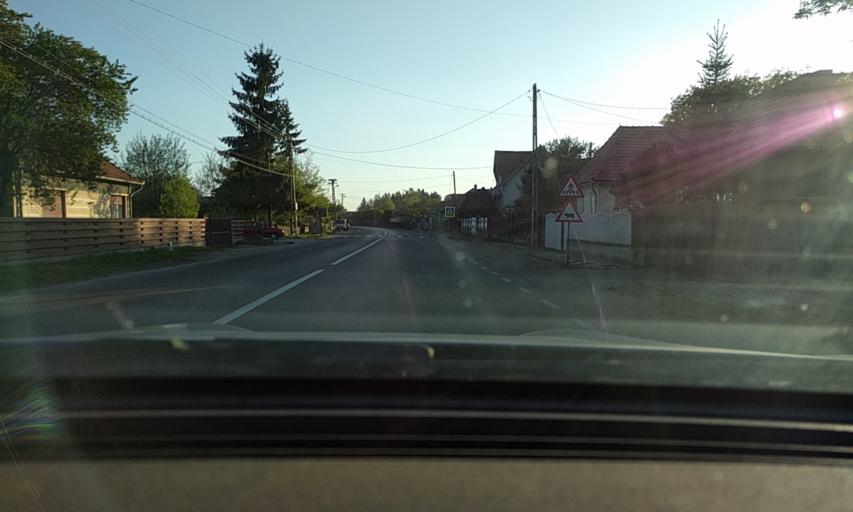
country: RO
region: Covasna
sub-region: Municipiul Targu Secuiesc
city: Lunga
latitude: 46.0258
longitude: 26.2246
